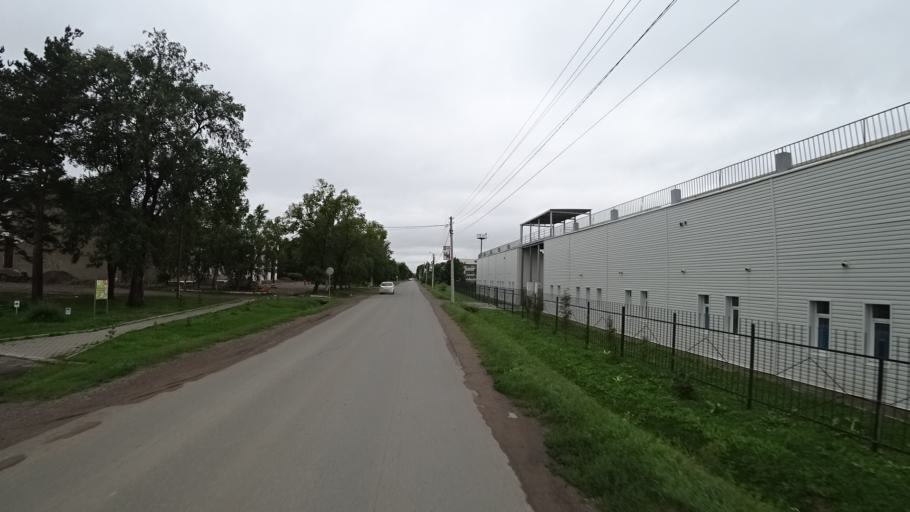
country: RU
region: Primorskiy
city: Chernigovka
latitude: 44.3422
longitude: 132.5728
